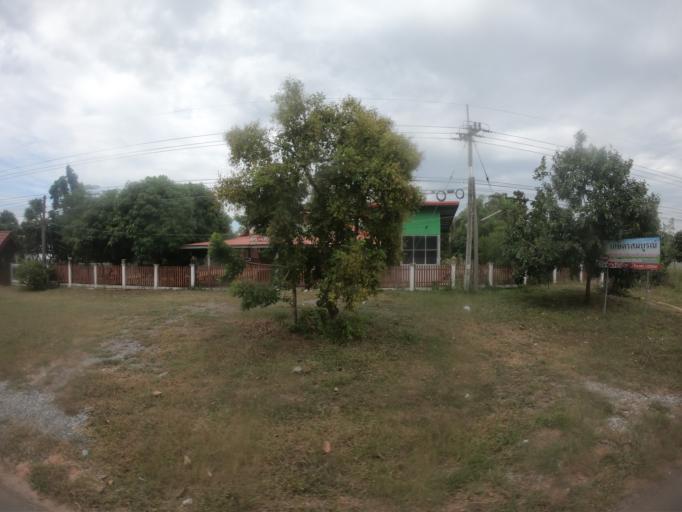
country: TH
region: Maha Sarakham
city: Kantharawichai
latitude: 16.3390
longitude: 103.1993
